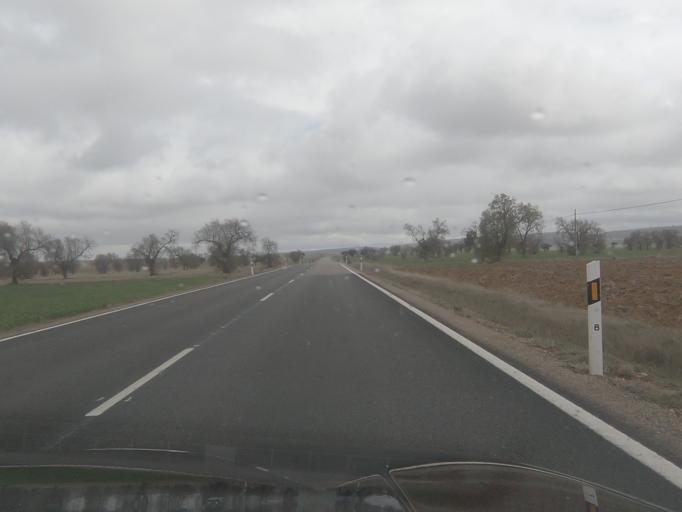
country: ES
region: Castille and Leon
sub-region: Provincia de Zamora
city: Pozuelo de Tabara
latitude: 41.7952
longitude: -5.9105
